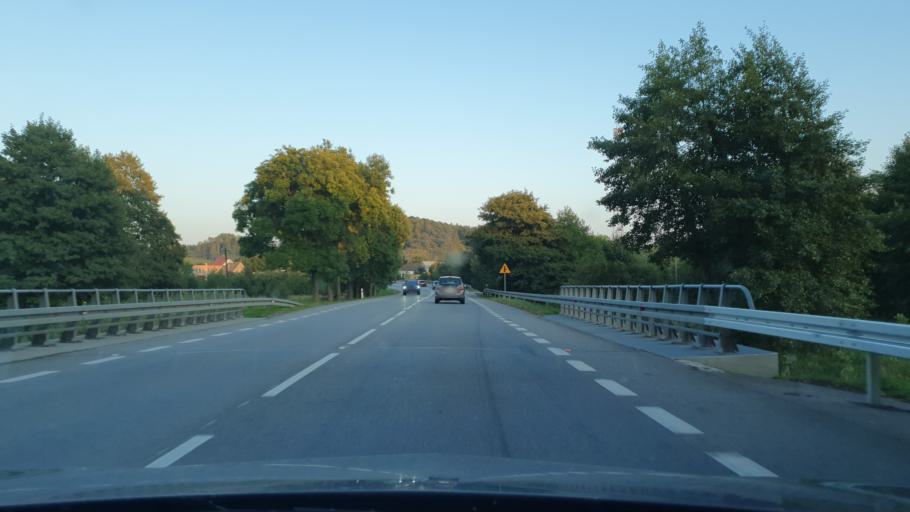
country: PL
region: Pomeranian Voivodeship
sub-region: Powiat leborski
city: Nowa Wies Leborska
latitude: 54.4998
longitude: 17.6295
